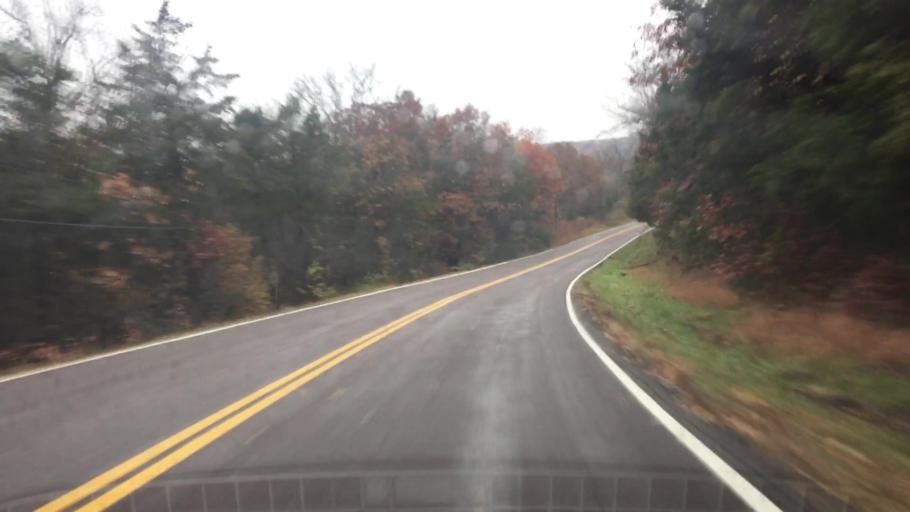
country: US
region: Missouri
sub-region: Boone County
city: Columbia
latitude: 38.8714
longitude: -92.3227
